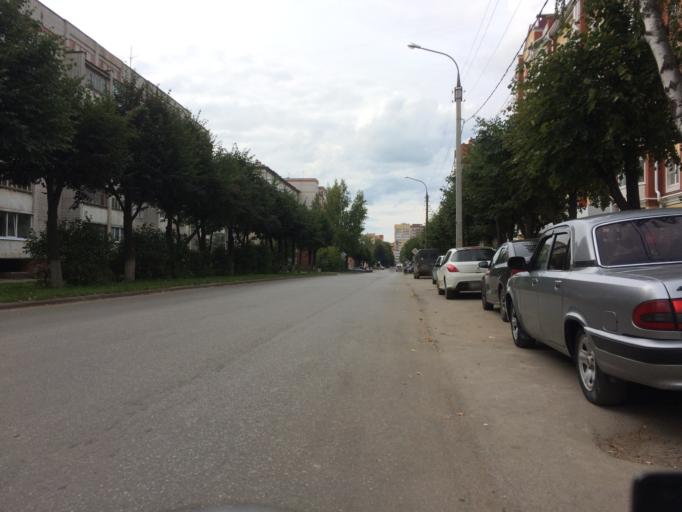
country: RU
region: Mariy-El
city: Yoshkar-Ola
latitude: 56.6361
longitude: 47.8701
